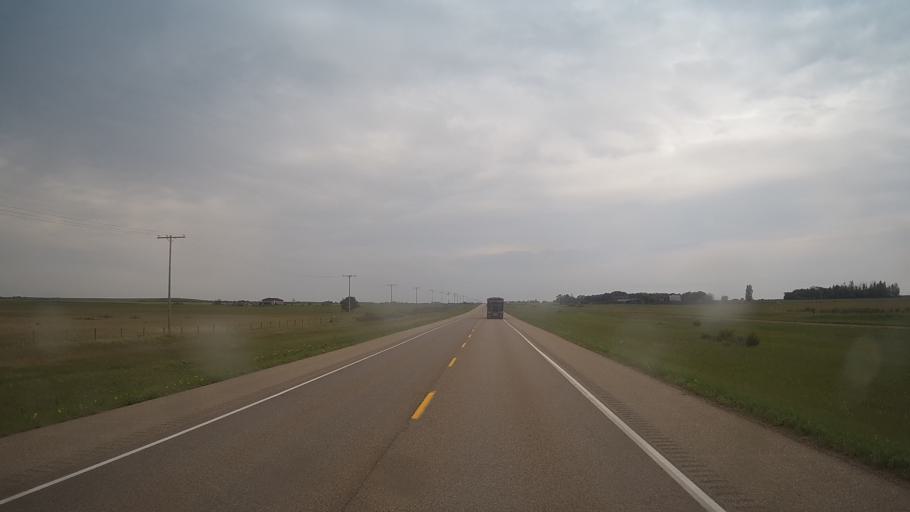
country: CA
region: Saskatchewan
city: Langham
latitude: 52.1290
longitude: -107.1589
